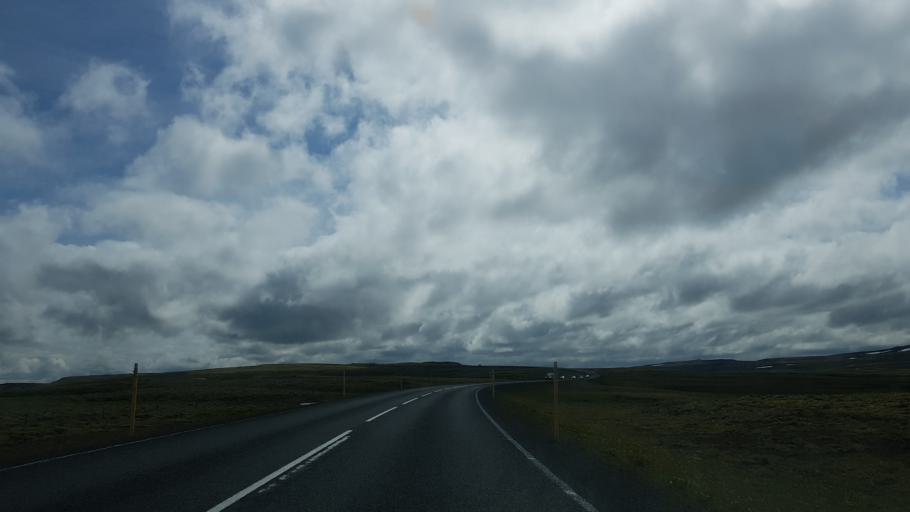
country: IS
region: West
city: Borgarnes
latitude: 65.0053
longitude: -21.0660
